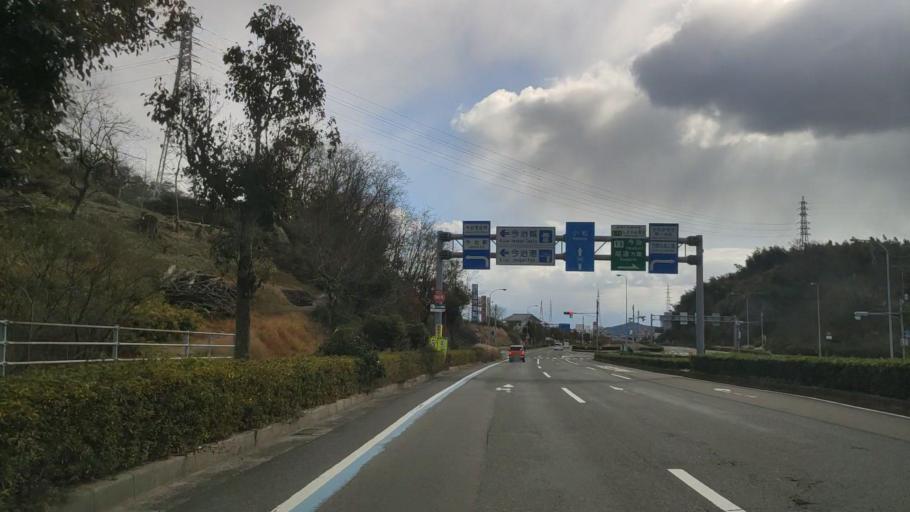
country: JP
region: Ehime
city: Hojo
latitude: 34.0560
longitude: 132.9756
